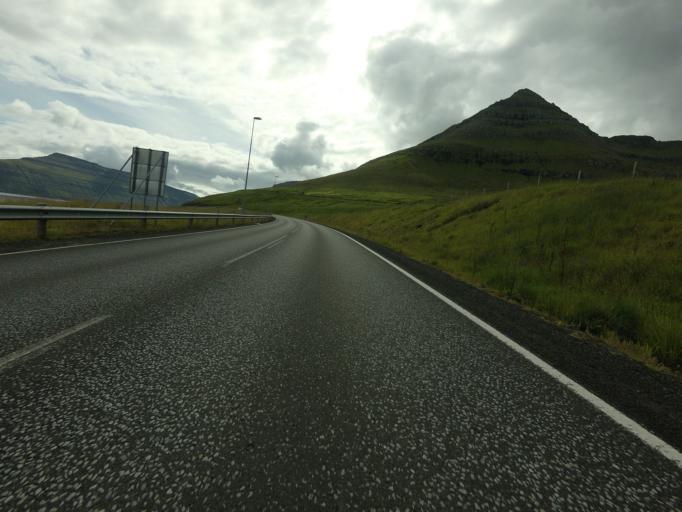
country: FO
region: Eysturoy
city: Eystur
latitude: 62.2096
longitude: -6.6972
